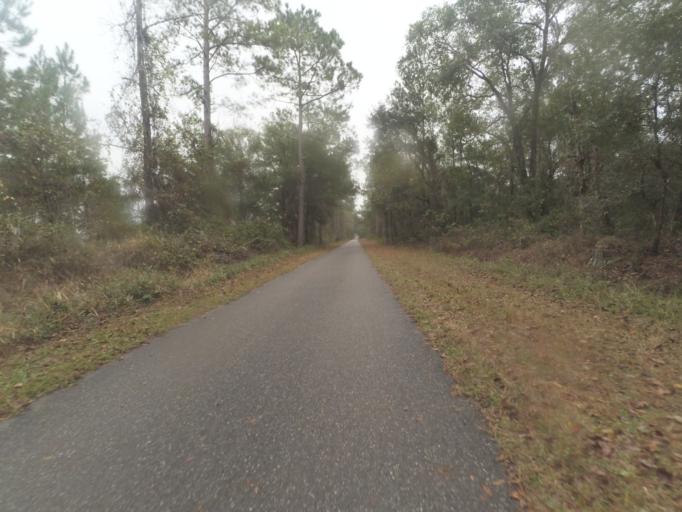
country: US
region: Florida
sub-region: Alachua County
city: Hawthorne
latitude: 29.5878
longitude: -82.1168
